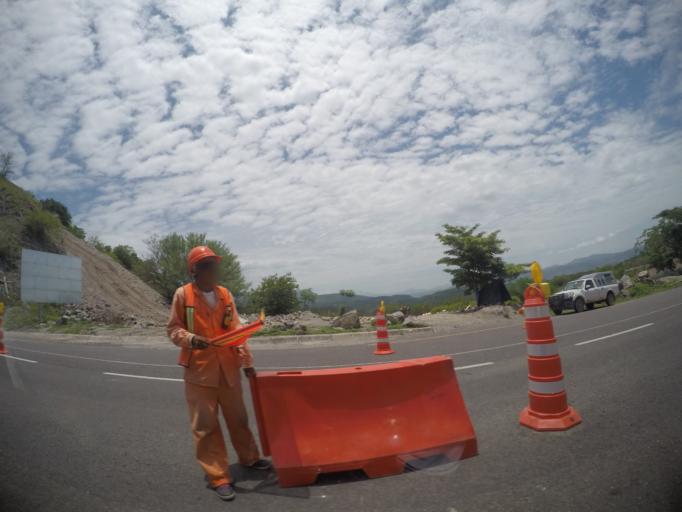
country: MX
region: Guerrero
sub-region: Huitzuco de los Figueroa
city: San Francisco Ozomatlan
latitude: 17.9253
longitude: -99.3738
